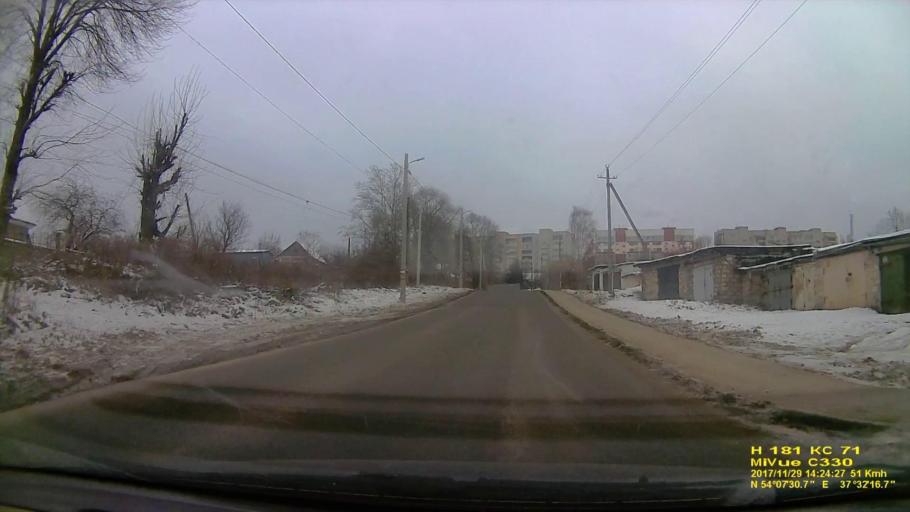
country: RU
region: Tula
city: Kosaya Gora
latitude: 54.1251
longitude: 37.5382
